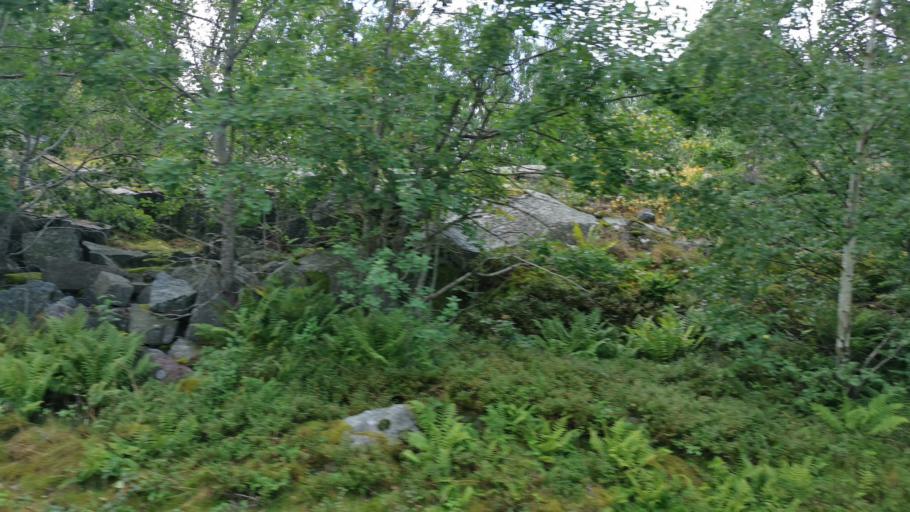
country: SE
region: Vaestra Goetaland
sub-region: Sotenas Kommun
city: Hunnebostrand
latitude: 58.5322
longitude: 11.2899
